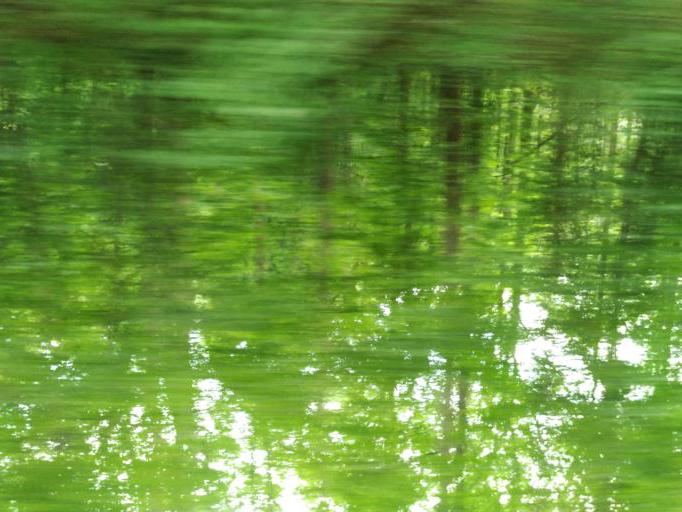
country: US
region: Maryland
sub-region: Anne Arundel County
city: Deale
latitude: 38.8294
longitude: -76.5870
